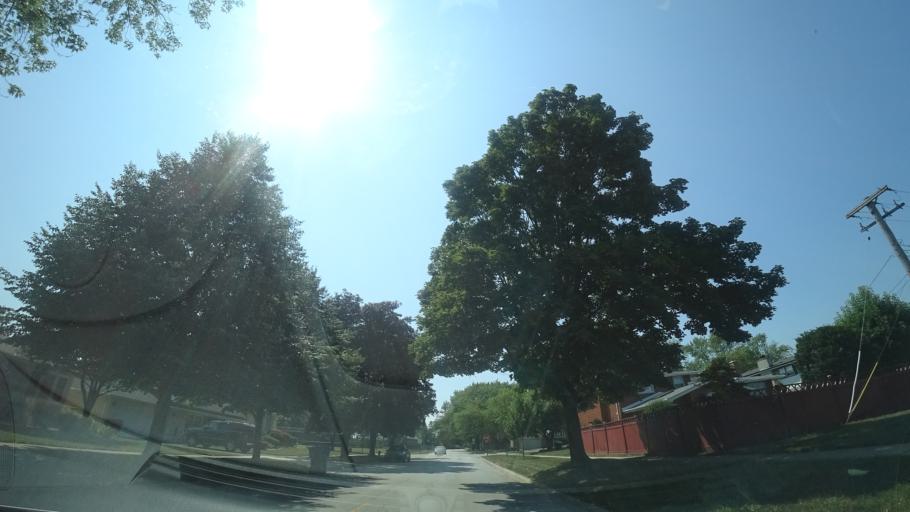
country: US
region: Illinois
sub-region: Cook County
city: Oak Lawn
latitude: 41.7017
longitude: -87.7540
